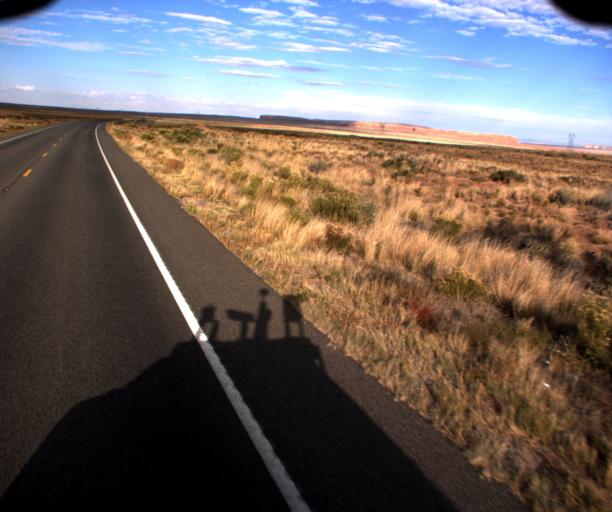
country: US
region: Arizona
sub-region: Apache County
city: Lukachukai
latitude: 36.9303
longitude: -109.2174
